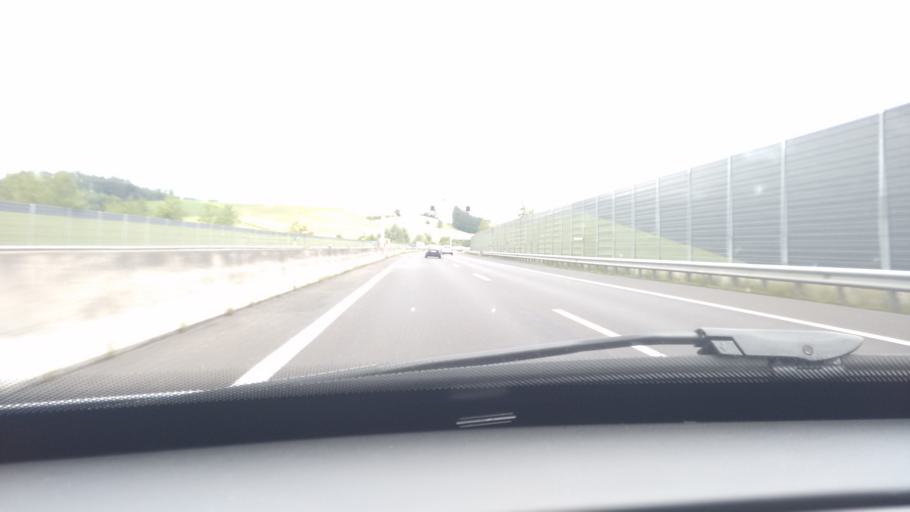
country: AT
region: Upper Austria
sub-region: Wels-Land
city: Offenhausen
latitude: 48.1775
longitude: 13.8390
